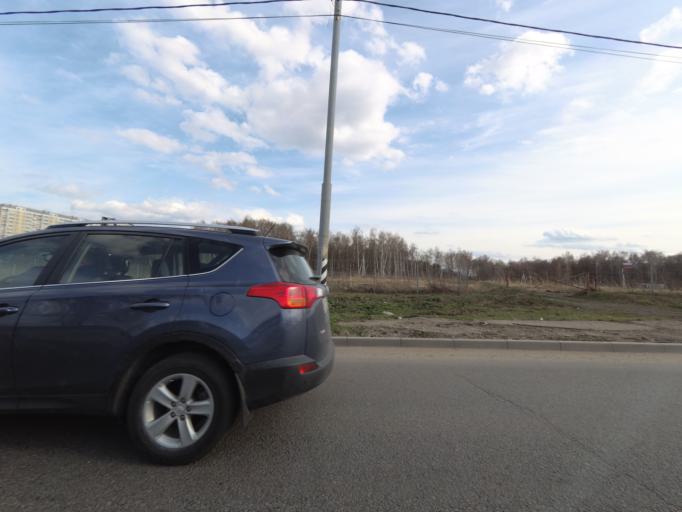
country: RU
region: Moskovskaya
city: Lobnya
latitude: 56.0052
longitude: 37.4316
